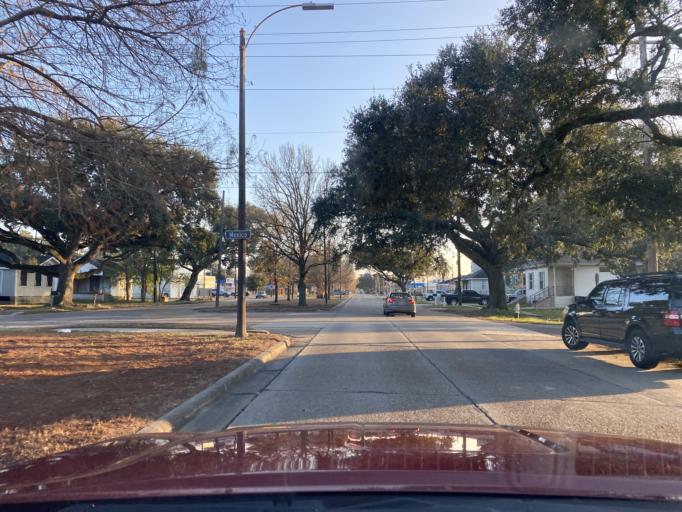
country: US
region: Louisiana
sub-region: Orleans Parish
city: New Orleans
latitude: 30.0240
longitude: -90.0521
